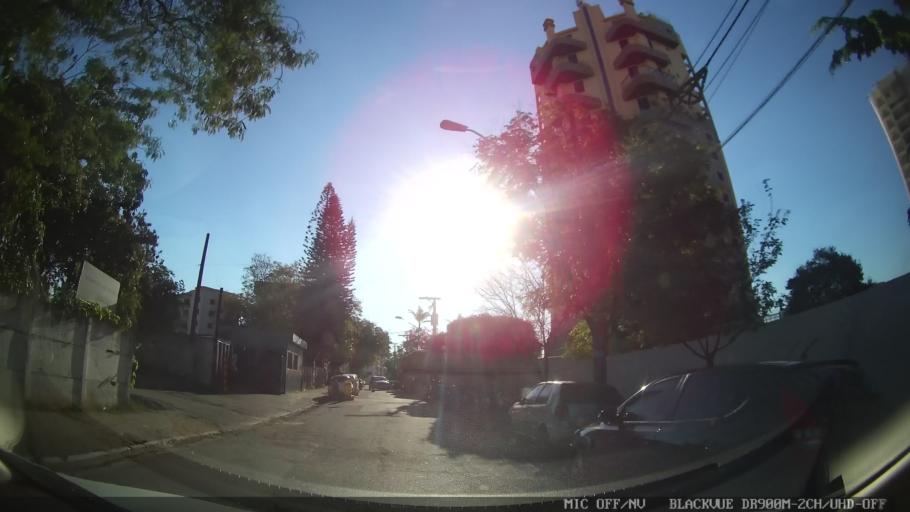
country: BR
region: Sao Paulo
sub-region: Sao Paulo
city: Sao Paulo
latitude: -23.4944
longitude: -46.6200
